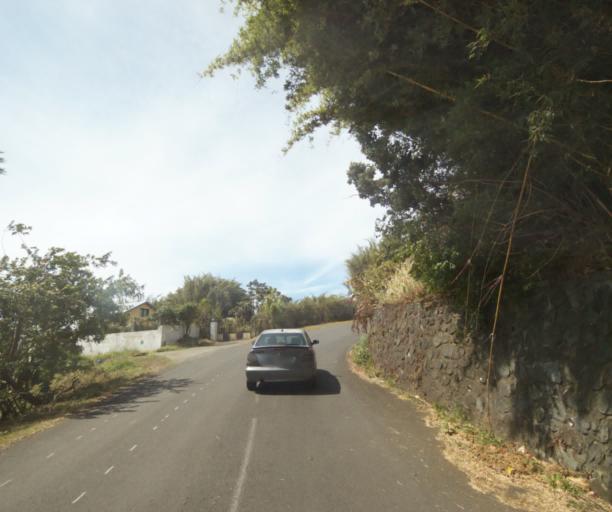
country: RE
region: Reunion
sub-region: Reunion
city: Saint-Paul
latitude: -21.0400
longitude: 55.3209
